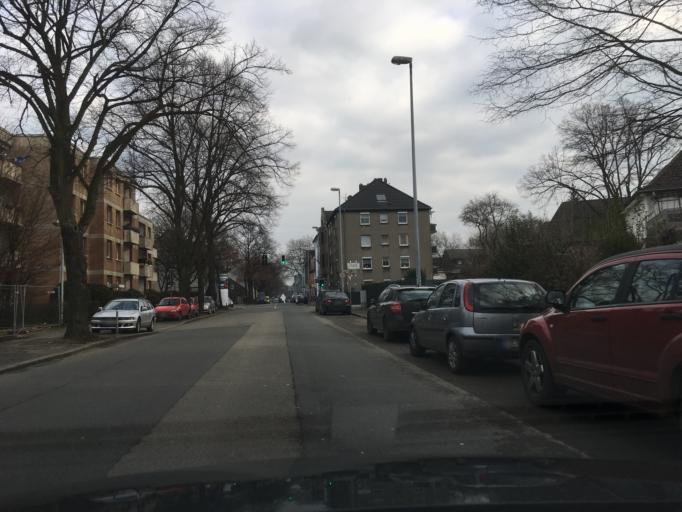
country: DE
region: North Rhine-Westphalia
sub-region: Regierungsbezirk Munster
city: Gladbeck
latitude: 51.5370
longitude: 7.0137
